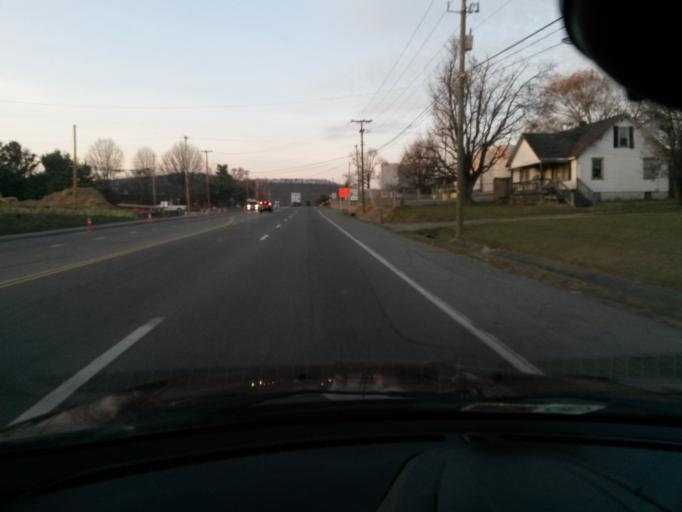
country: US
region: Virginia
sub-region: Roanoke County
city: Hollins
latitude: 37.3516
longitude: -79.9535
